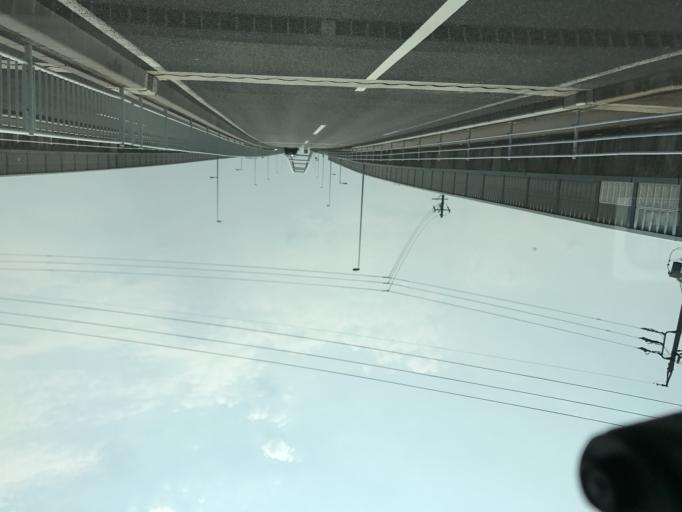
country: JP
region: Aichi
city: Kanie
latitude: 35.1024
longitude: 136.8426
